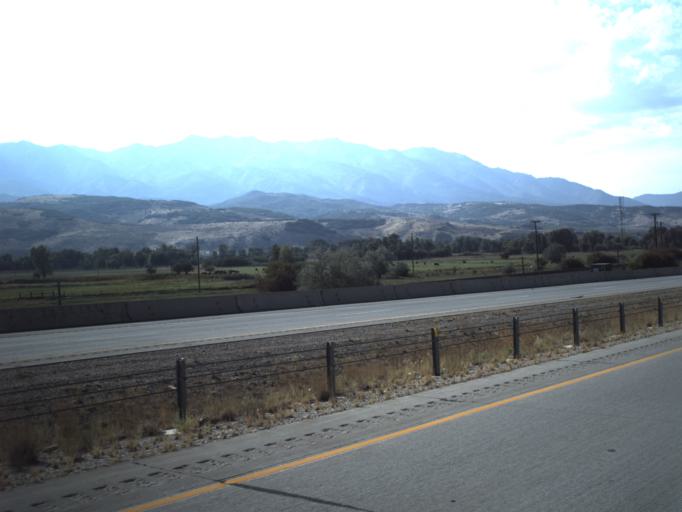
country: US
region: Utah
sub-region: Morgan County
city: Morgan
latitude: 41.0743
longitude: -111.7195
